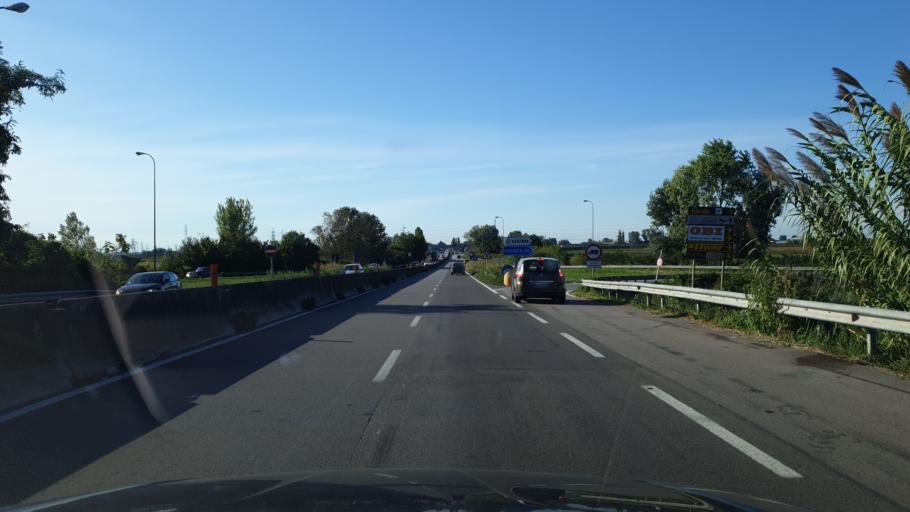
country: IT
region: Emilia-Romagna
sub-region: Provincia di Ravenna
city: Fornace Zarattini
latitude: 44.4233
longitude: 12.1612
